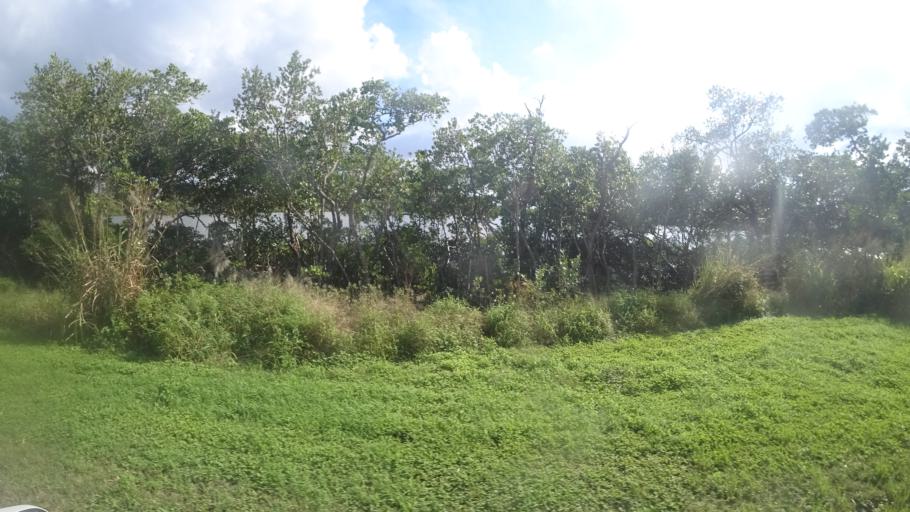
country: US
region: Florida
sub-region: Manatee County
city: Memphis
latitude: 27.5751
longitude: -82.5867
